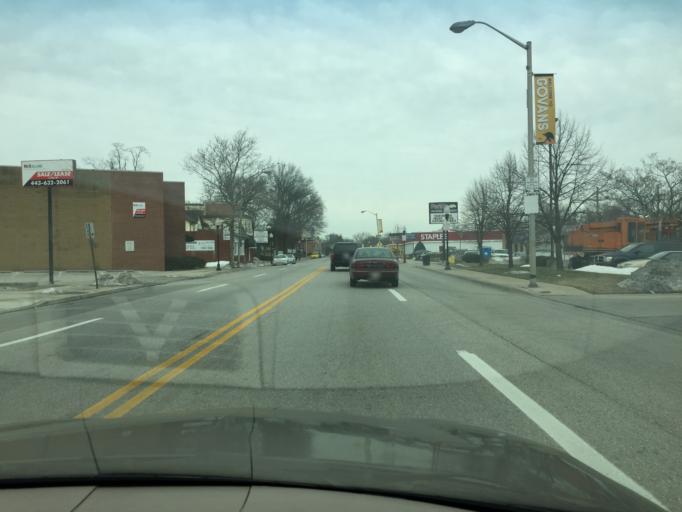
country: US
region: Maryland
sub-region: Baltimore County
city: Towson
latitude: 39.3607
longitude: -76.6099
